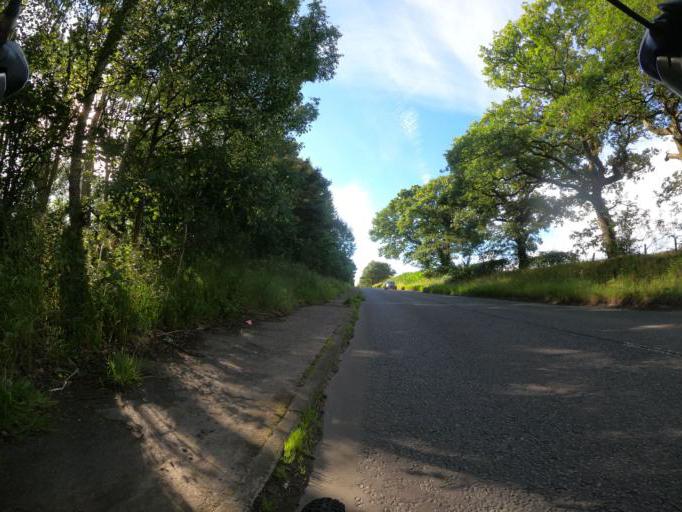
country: GB
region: Scotland
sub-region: Edinburgh
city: Newbridge
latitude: 55.9239
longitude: -3.4138
